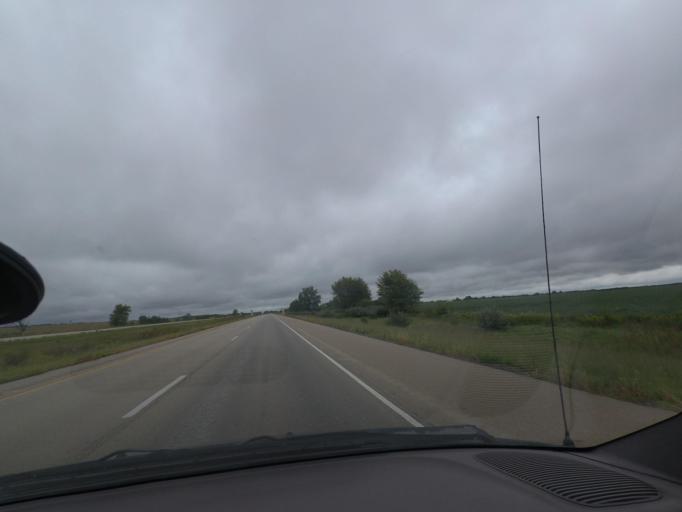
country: US
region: Illinois
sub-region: Piatt County
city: Cerro Gordo
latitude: 39.9606
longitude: -88.8182
